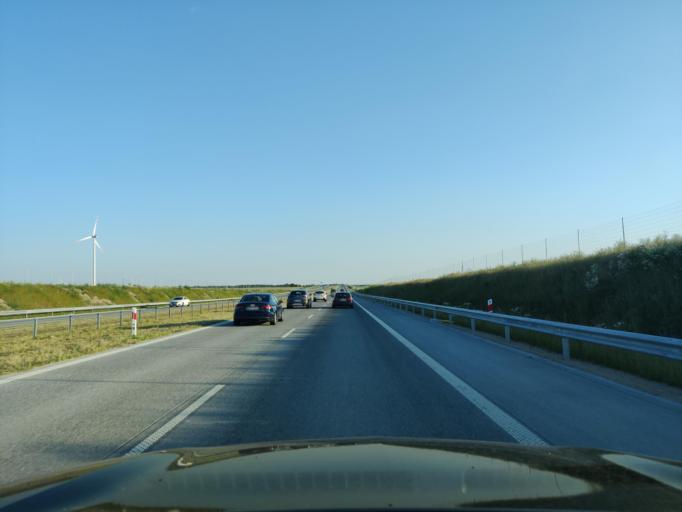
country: PL
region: Masovian Voivodeship
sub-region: Powiat mlawski
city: Wisniewo
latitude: 53.0580
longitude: 20.3643
